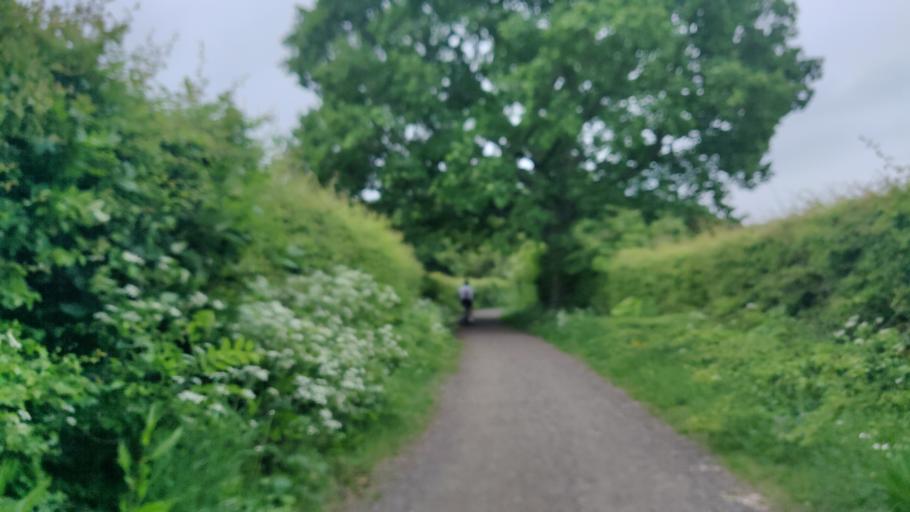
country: GB
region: England
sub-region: West Sussex
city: Southwater
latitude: 51.0436
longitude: -0.3695
